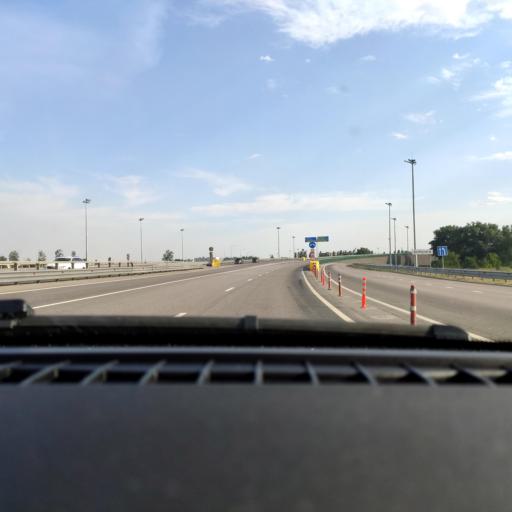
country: RU
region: Voronezj
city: Somovo
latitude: 51.6555
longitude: 39.3029
